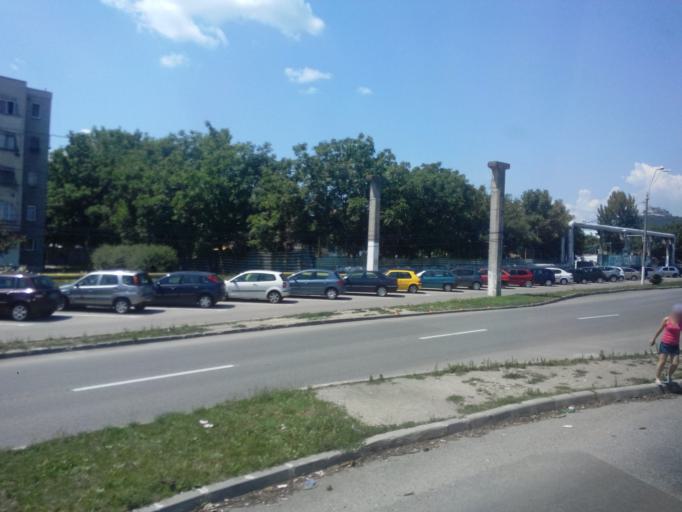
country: RO
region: Hunedoara
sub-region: Municipiul Deva
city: Deva
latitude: 45.8724
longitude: 22.9186
